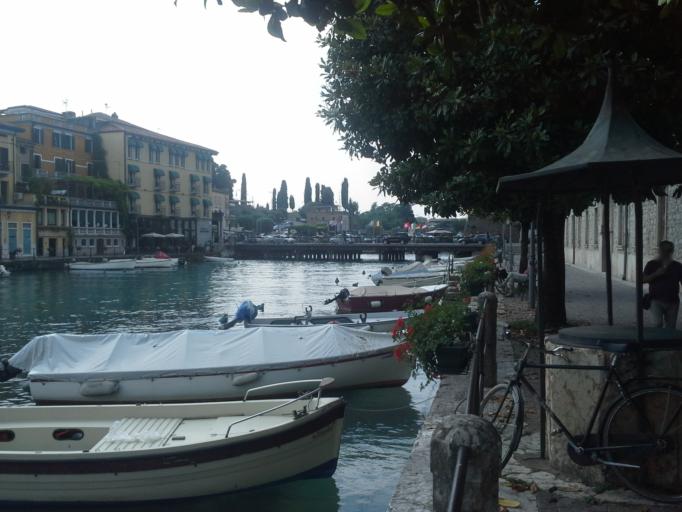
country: IT
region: Veneto
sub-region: Provincia di Verona
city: Peschiera del Garda
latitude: 45.4392
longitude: 10.6943
